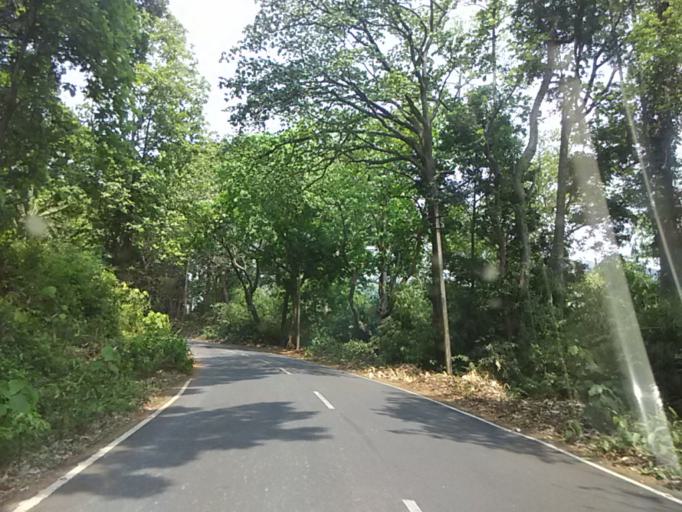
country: IN
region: Karnataka
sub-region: Kodagu
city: Virarajendrapet
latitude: 12.0732
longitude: 75.7266
